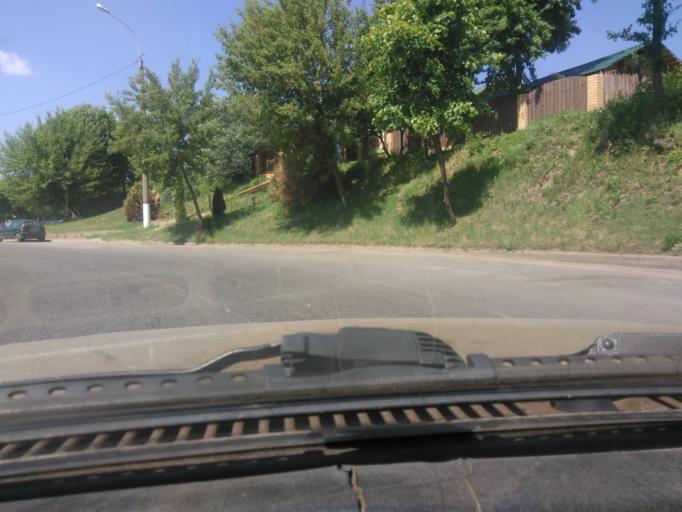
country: BY
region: Mogilev
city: Mahilyow
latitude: 53.9185
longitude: 30.3767
